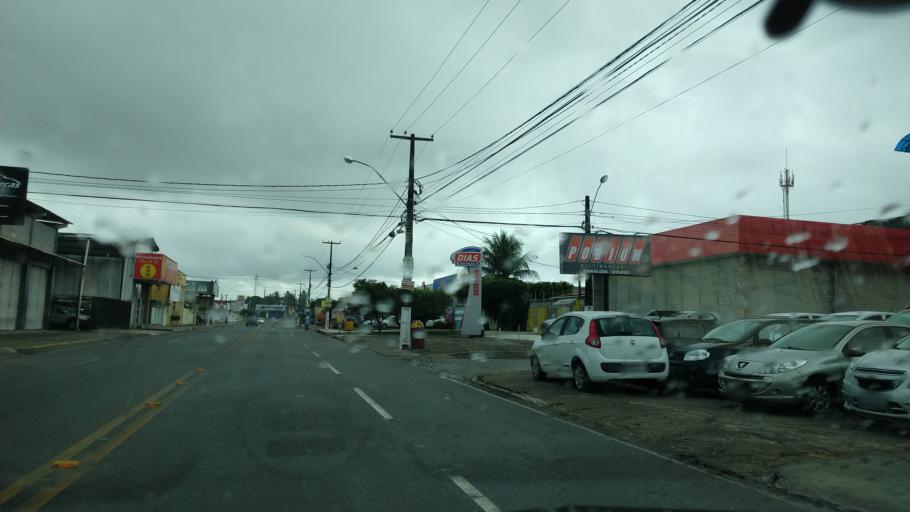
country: BR
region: Rio Grande do Norte
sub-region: Parnamirim
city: Parnamirim
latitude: -5.9280
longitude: -35.2679
